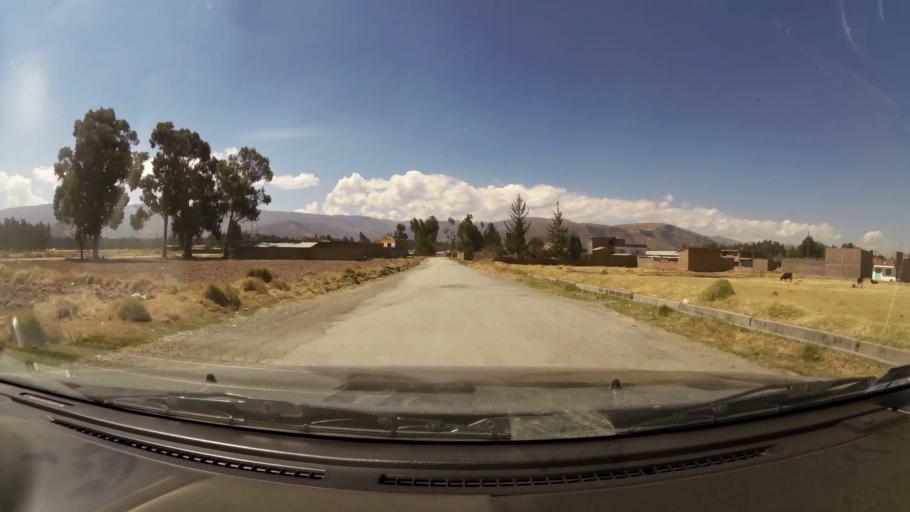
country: PE
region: Junin
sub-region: Provincia de Jauja
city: Jauja
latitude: -11.7676
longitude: -75.4951
